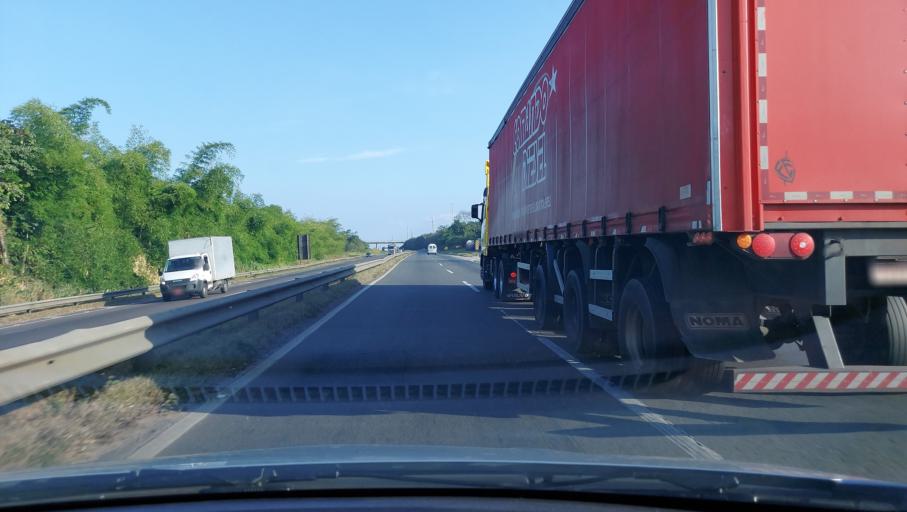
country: BR
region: Bahia
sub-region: Conceicao Do Jacuipe
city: Conceicao do Jacuipe
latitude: -12.3562
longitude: -38.8293
